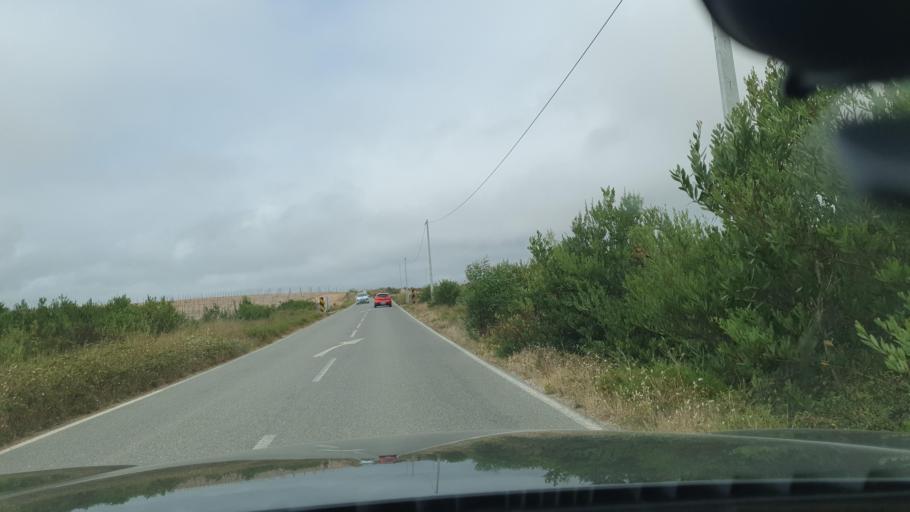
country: PT
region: Beja
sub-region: Odemira
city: Sao Teotonio
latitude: 37.5467
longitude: -8.7456
